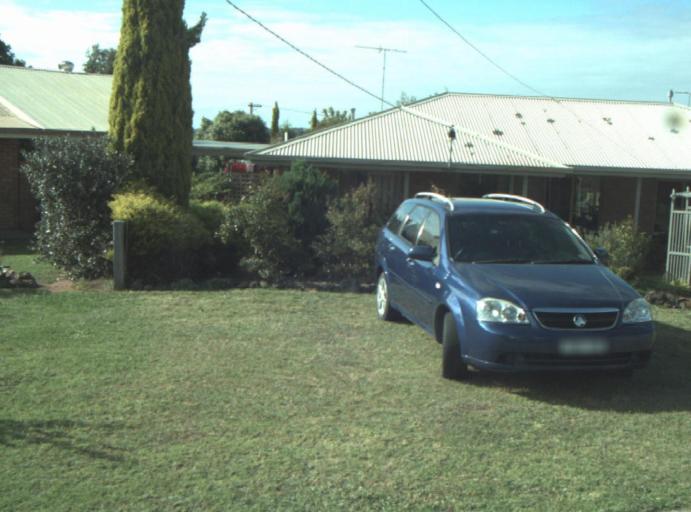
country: AU
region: Victoria
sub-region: Greater Geelong
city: Wandana Heights
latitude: -38.2121
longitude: 144.3174
